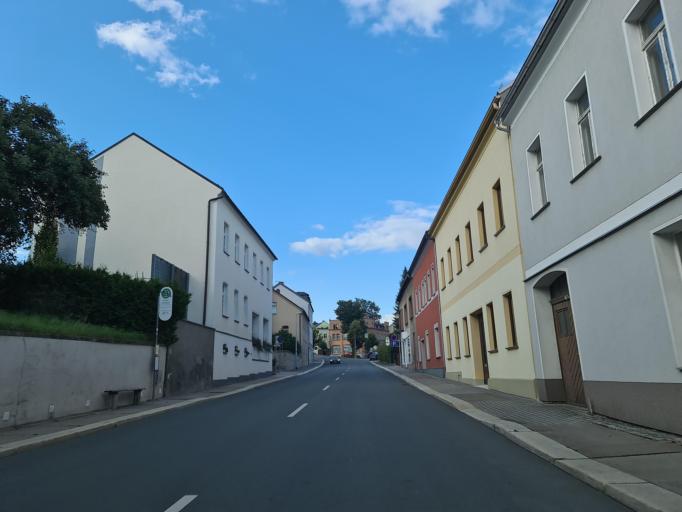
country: DE
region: Saxony
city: Pausa
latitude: 50.5822
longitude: 11.9973
